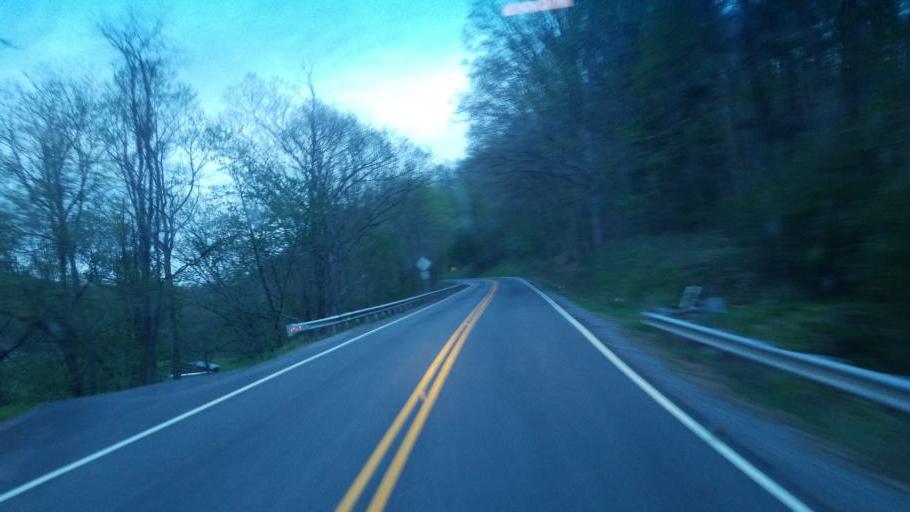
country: US
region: Virginia
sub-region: Smyth County
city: Atkins
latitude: 36.8175
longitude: -81.4440
